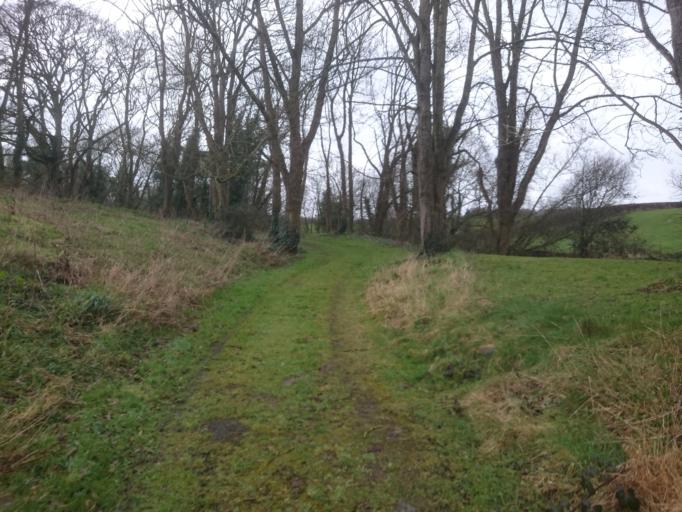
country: IE
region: Leinster
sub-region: Laois
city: Abbeyleix
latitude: 52.8475
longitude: -7.4021
